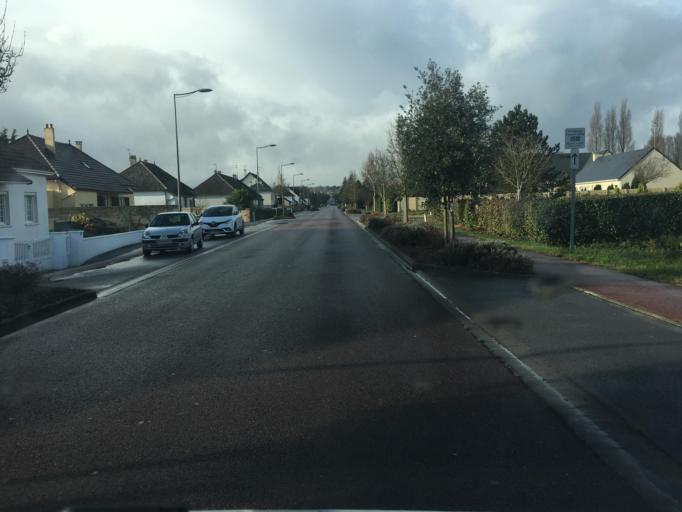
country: FR
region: Lower Normandy
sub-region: Departement de la Manche
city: Quettehou
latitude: 49.5905
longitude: -1.2902
